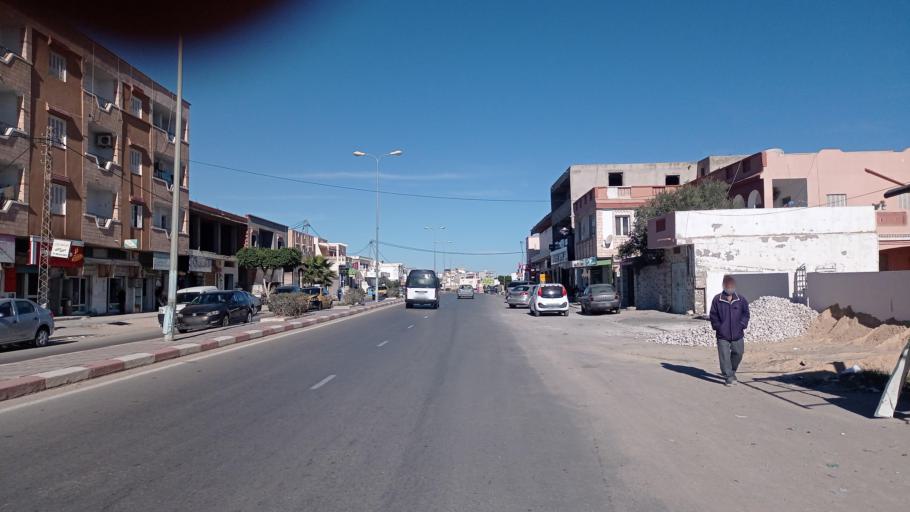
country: TN
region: Qabis
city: Gabes
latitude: 33.8469
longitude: 10.1129
